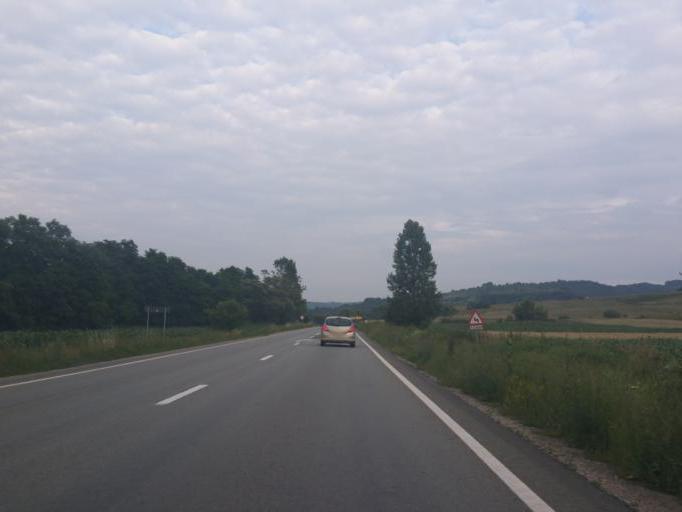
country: RO
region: Salaj
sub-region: Comuna Sanmihaiu Almasului
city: Sanmihaiu Almasului
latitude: 46.9604
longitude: 23.3237
